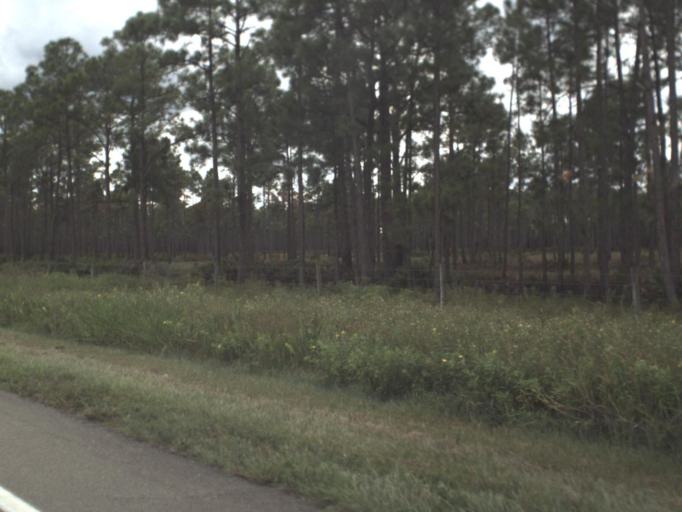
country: US
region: Florida
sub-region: Lee County
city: Olga
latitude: 26.8811
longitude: -81.7600
